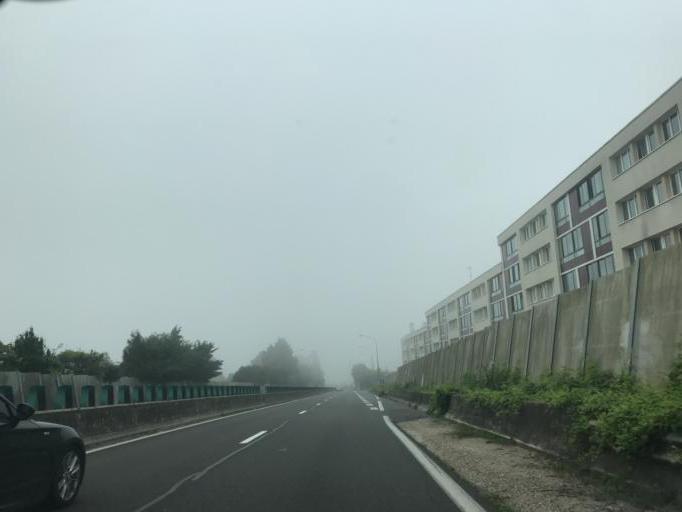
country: FR
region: Ile-de-France
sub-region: Departement de Seine-et-Marne
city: Lagny-sur-Marne
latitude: 48.8741
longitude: 2.7186
